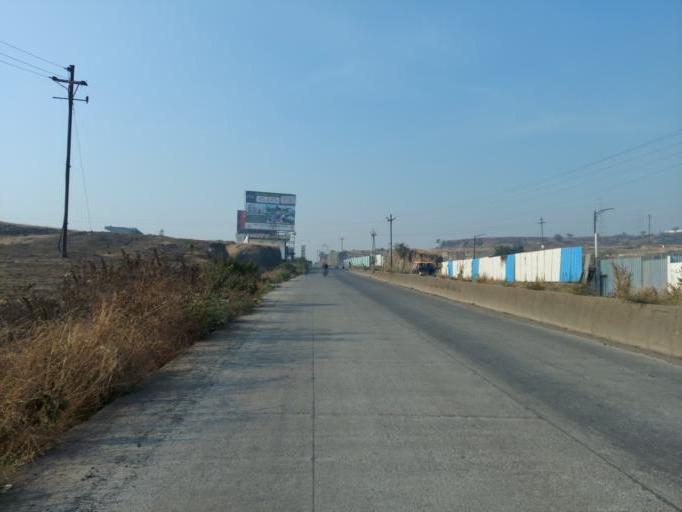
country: IN
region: Maharashtra
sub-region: Pune Division
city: Pune
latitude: 18.4610
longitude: 73.9498
